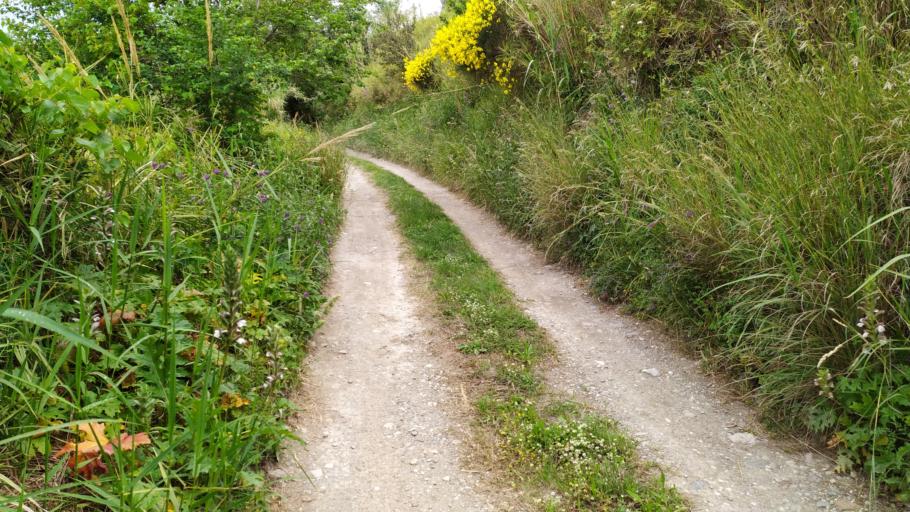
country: IT
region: Sicily
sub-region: Messina
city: Pace del Mela
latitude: 38.1623
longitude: 15.2945
